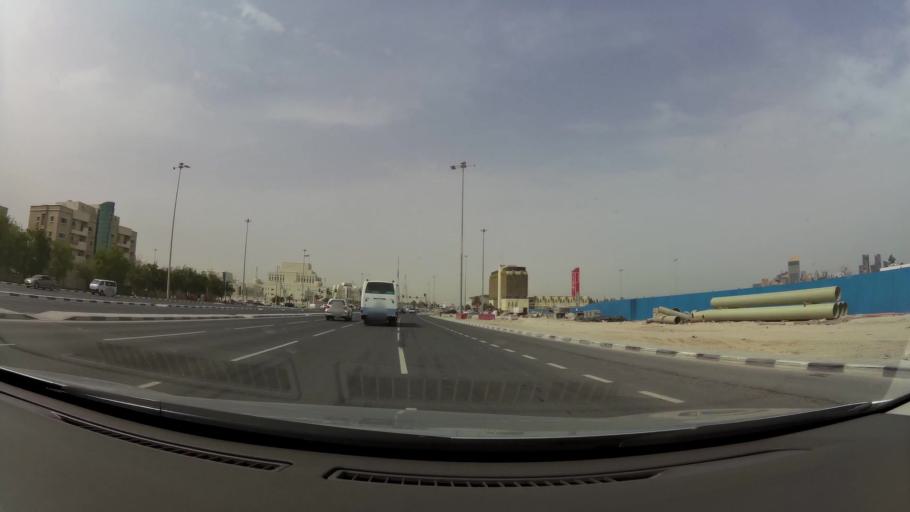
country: QA
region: Baladiyat ad Dawhah
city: Doha
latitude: 25.3003
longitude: 51.5078
